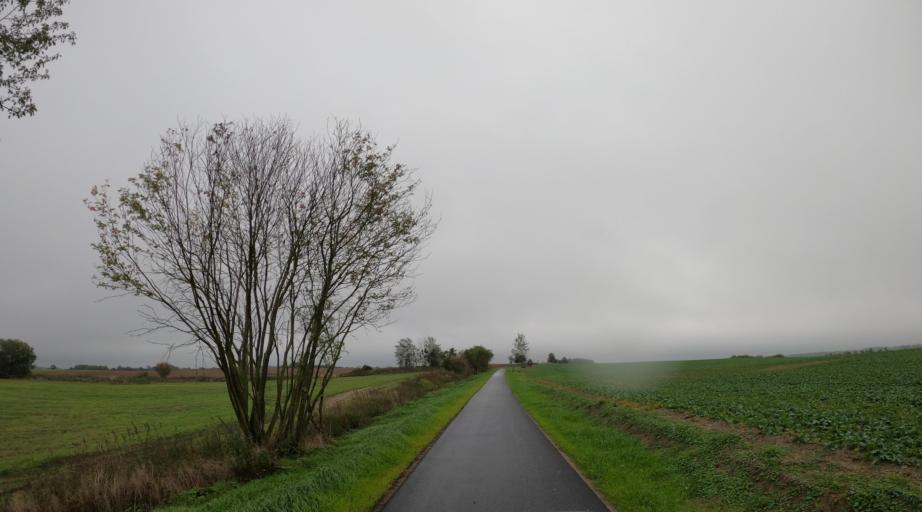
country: PL
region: West Pomeranian Voivodeship
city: Trzcinsko Zdroj
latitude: 52.9258
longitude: 14.7318
